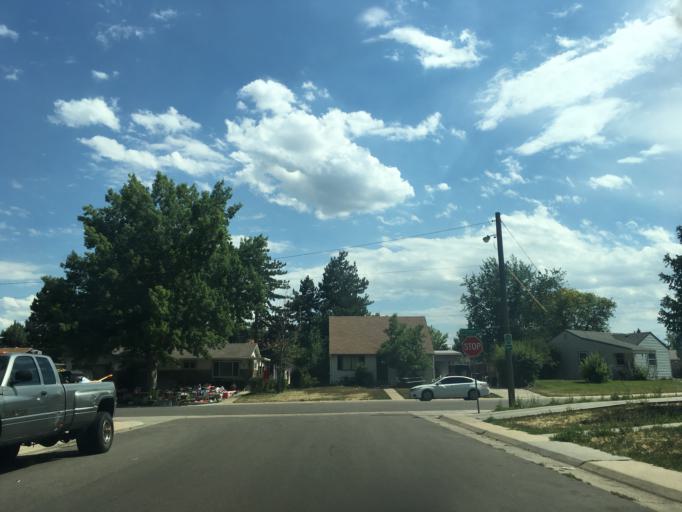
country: US
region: Colorado
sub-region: Jefferson County
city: Lakewood
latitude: 39.6866
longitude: -105.0521
